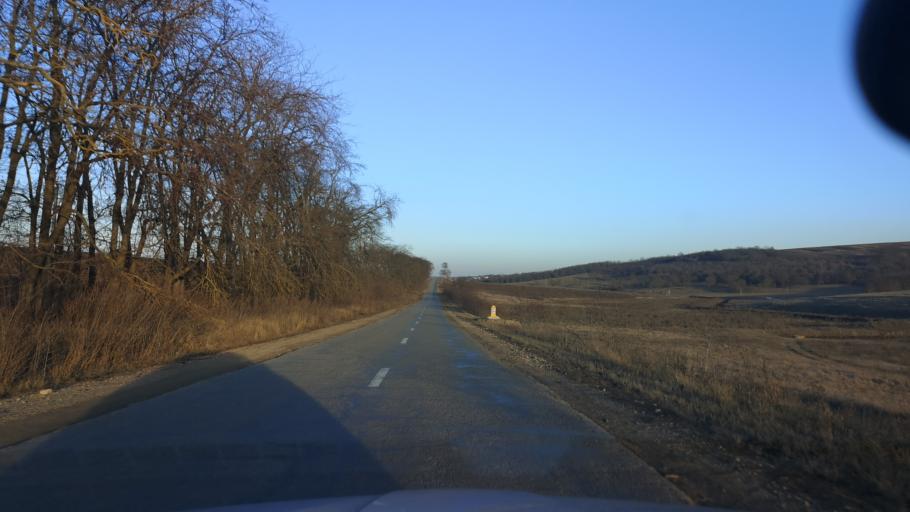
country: MD
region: Orhei
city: Orhei
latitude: 47.2963
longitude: 28.9031
